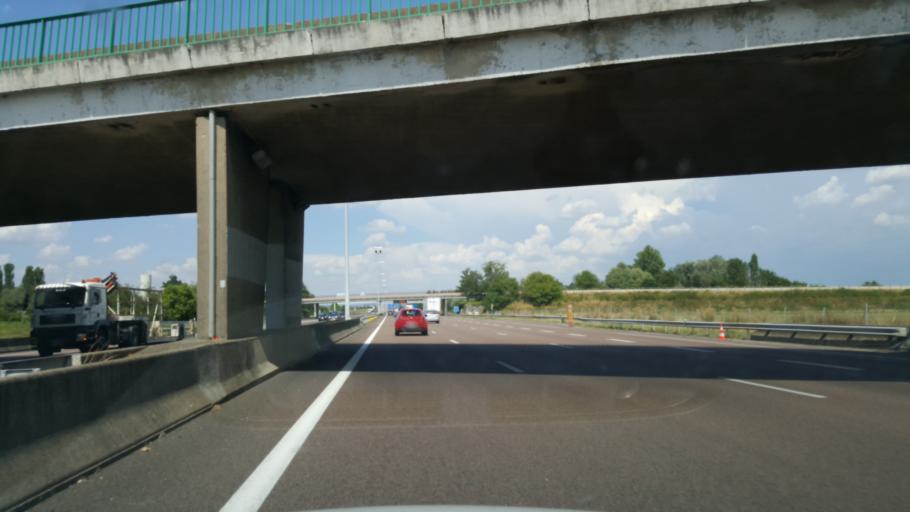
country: FR
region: Bourgogne
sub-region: Departement de la Cote-d'Or
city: Bligny-les-Beaune
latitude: 46.9997
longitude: 4.8593
